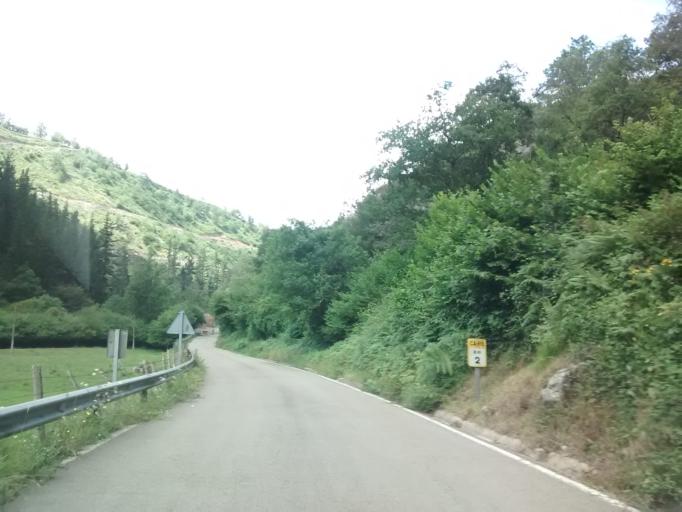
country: ES
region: Cantabria
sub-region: Provincia de Cantabria
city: Ruente
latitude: 43.1937
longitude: -4.2853
